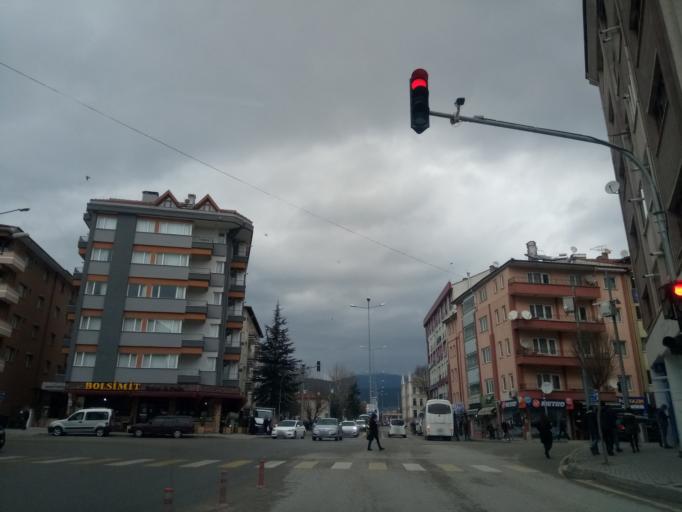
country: TR
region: Bolu
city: Bolu
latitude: 40.7013
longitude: 31.5797
